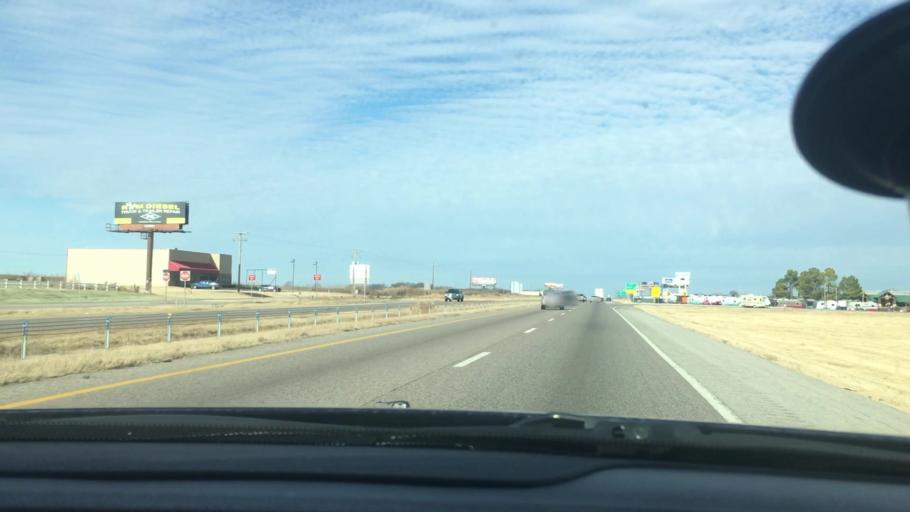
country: US
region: Oklahoma
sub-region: McClain County
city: Goldsby
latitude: 35.1543
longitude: -97.4777
